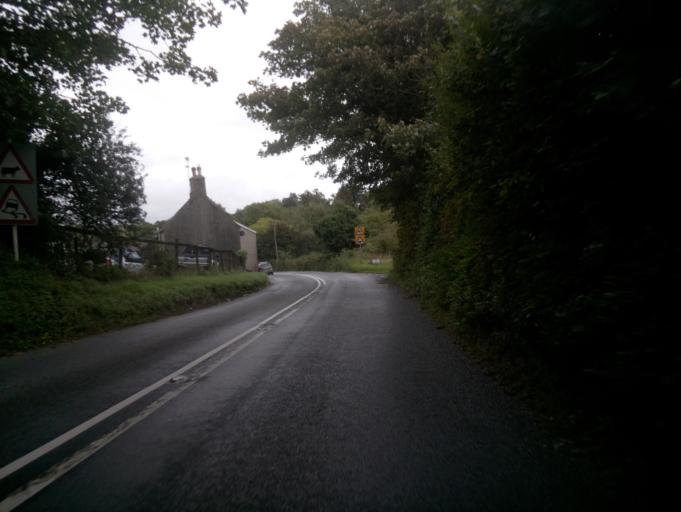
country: GB
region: England
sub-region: Devon
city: Modbury
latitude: 50.3395
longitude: -3.8646
